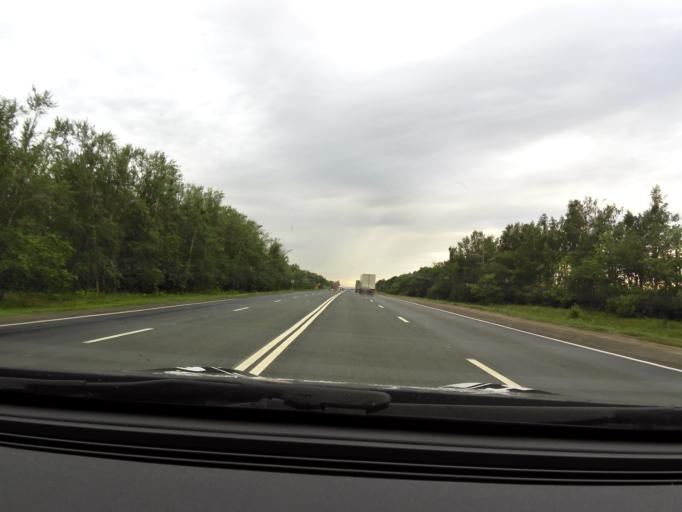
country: RU
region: Chuvashia
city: Yantikovo
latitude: 55.8089
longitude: 48.0342
